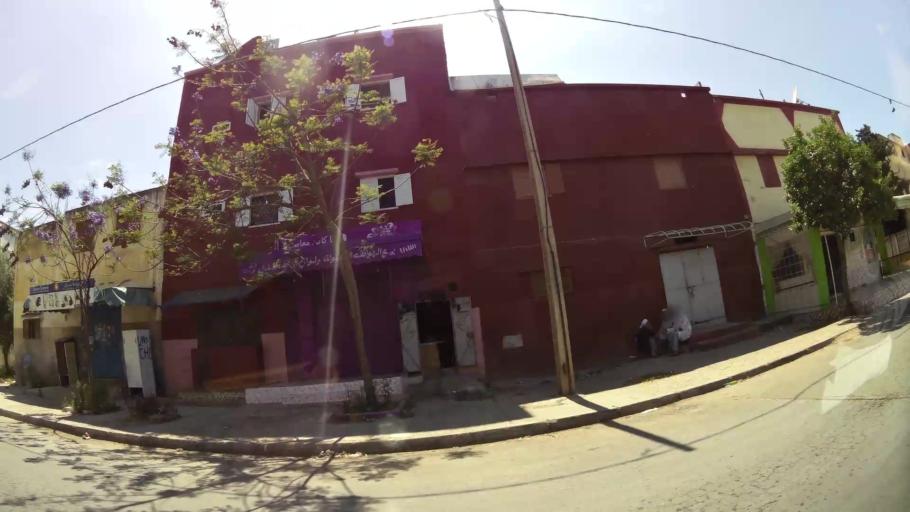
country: MA
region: Gharb-Chrarda-Beni Hssen
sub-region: Kenitra Province
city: Kenitra
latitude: 34.2488
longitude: -6.5449
